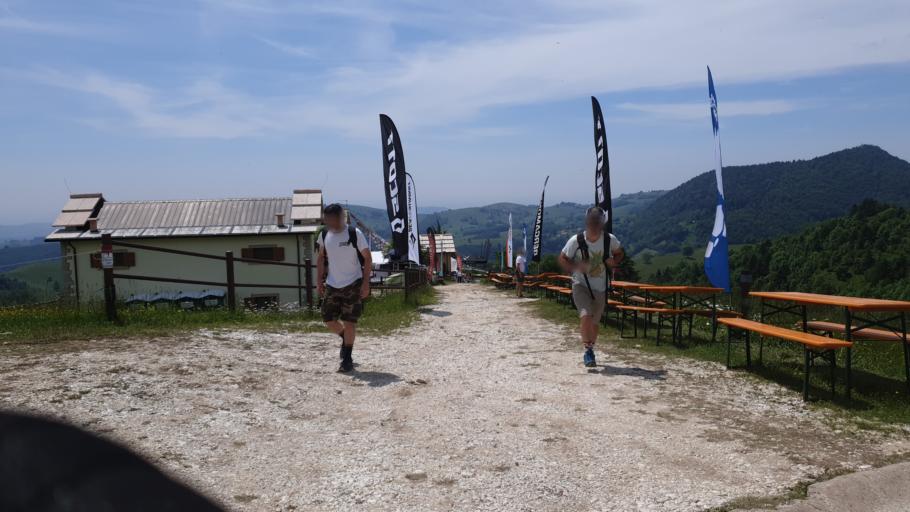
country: IT
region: Veneto
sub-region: Provincia di Verona
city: Selva di Progno
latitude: 45.6293
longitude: 11.1163
